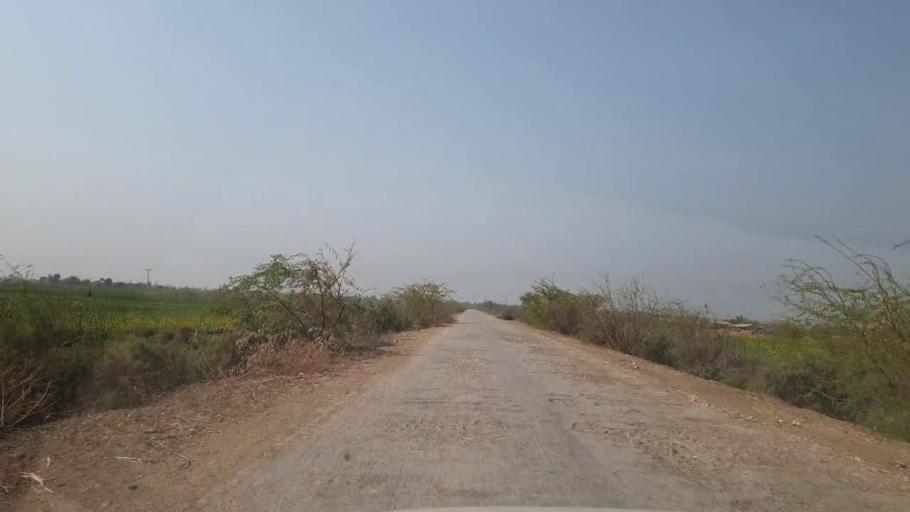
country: PK
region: Sindh
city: Mirpur Khas
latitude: 25.6988
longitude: 69.1446
